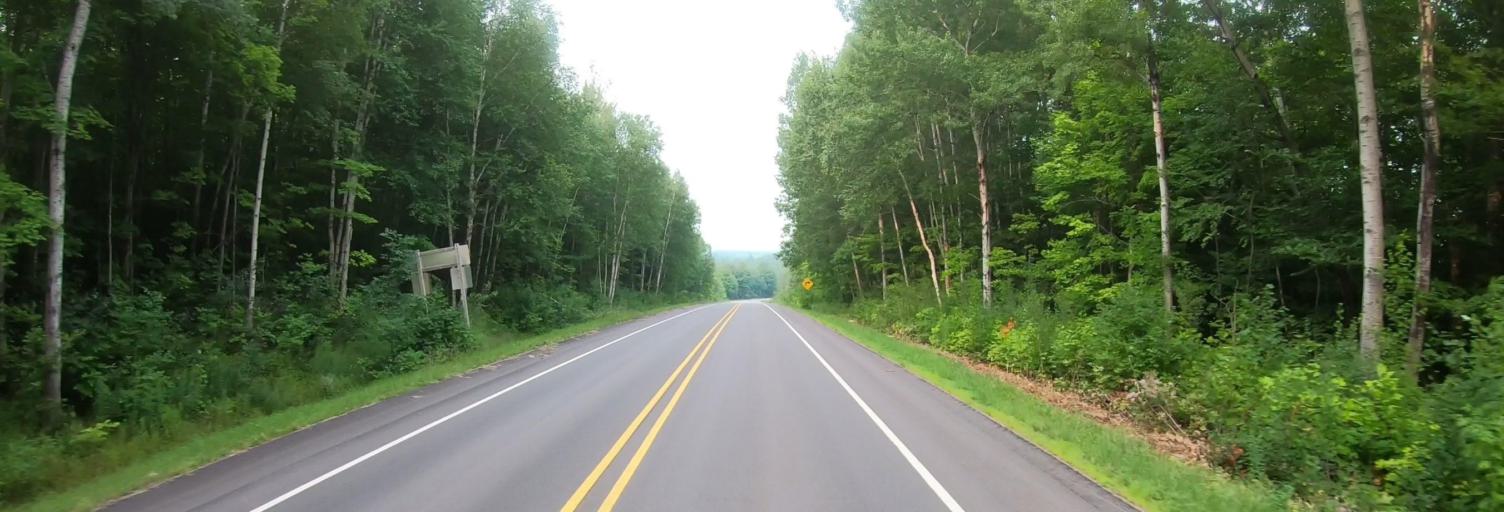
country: US
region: Michigan
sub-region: Luce County
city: Newberry
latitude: 46.4724
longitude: -84.9578
